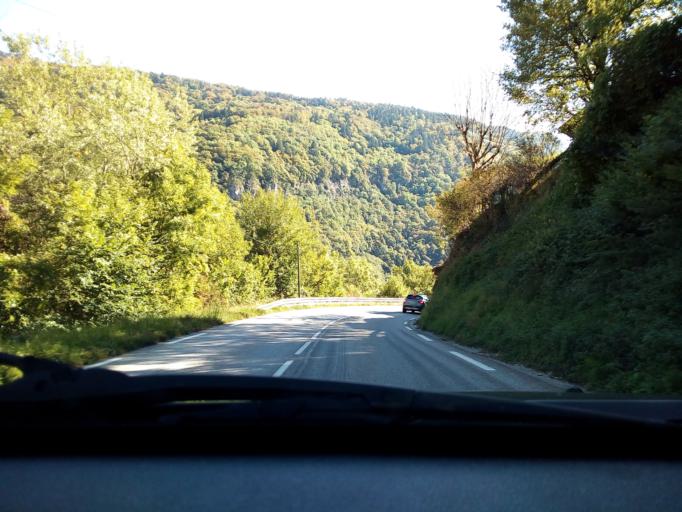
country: FR
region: Rhone-Alpes
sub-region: Departement de l'Isere
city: Sassenage
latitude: 45.2040
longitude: 5.6333
